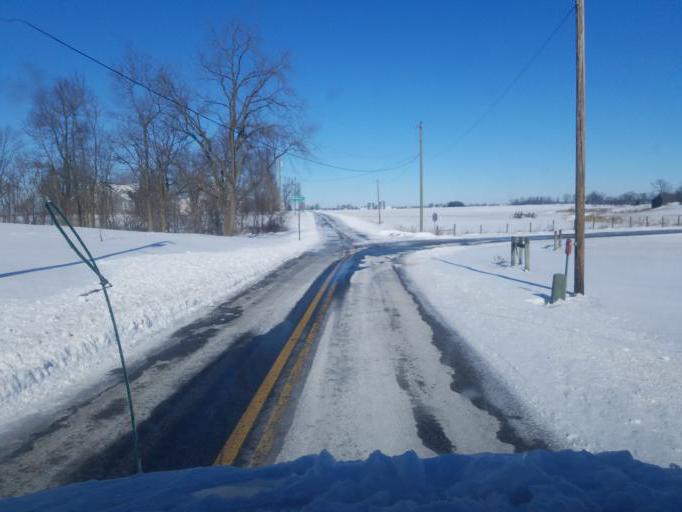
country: US
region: Ohio
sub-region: Delaware County
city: Delaware
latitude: 40.3036
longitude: -82.9886
